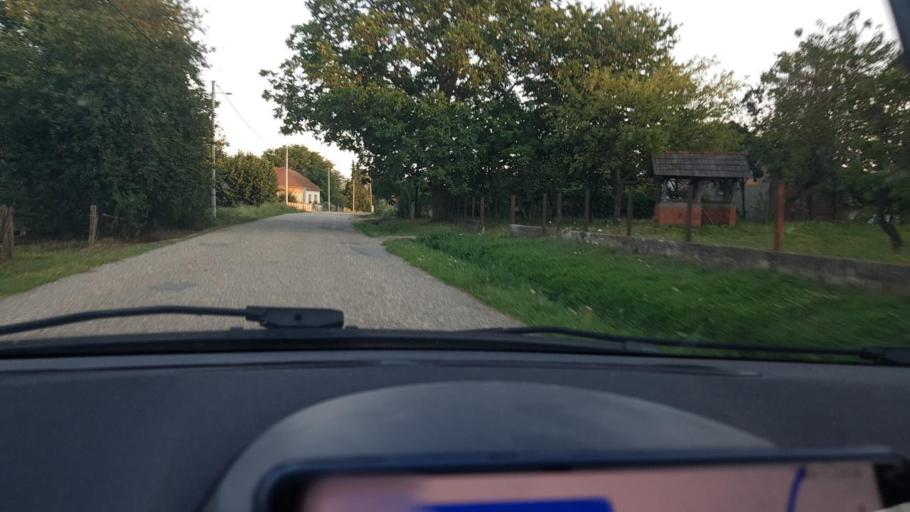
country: HR
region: Bjelovarsko-Bilogorska
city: Zdralovi
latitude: 45.8729
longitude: 17.0011
